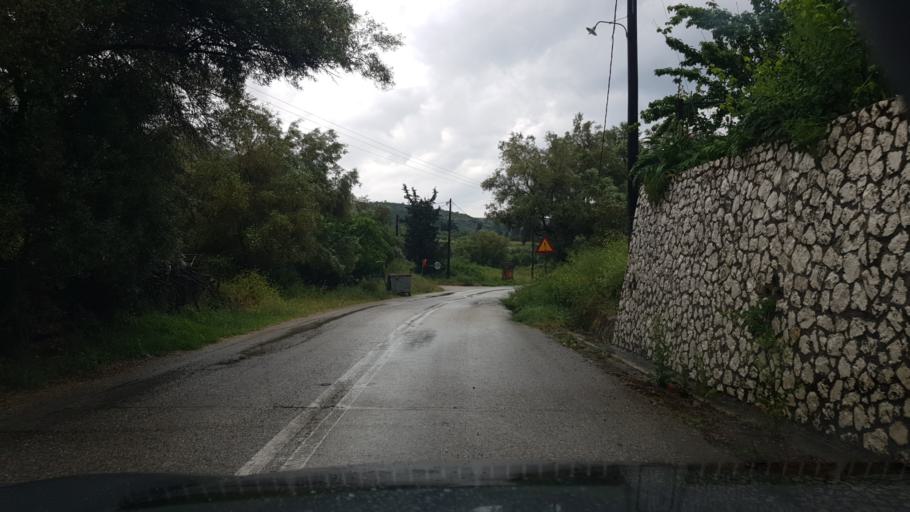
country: GR
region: Ionian Islands
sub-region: Lefkada
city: Nidri
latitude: 38.6291
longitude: 20.6306
